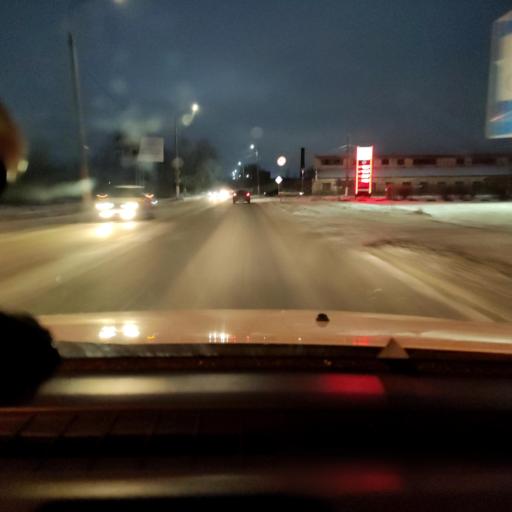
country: RU
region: Samara
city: Chapayevsk
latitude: 52.9653
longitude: 49.6931
